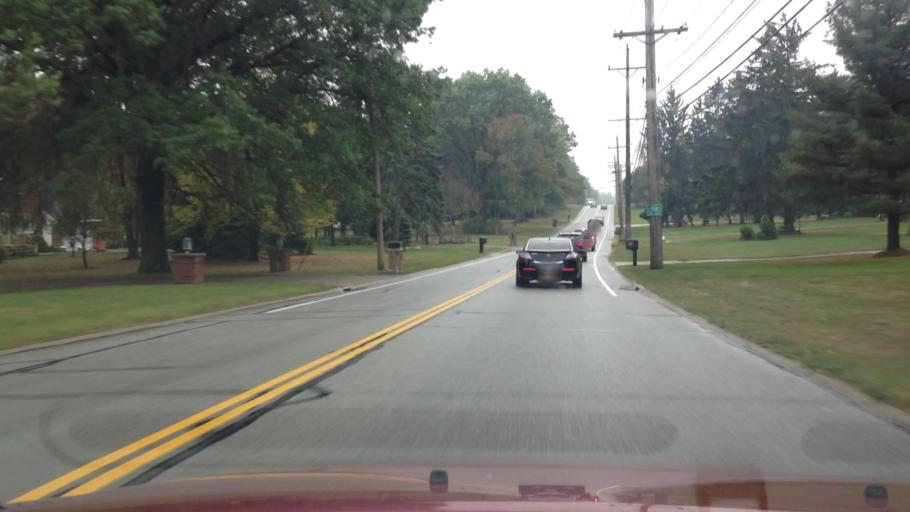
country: US
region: Ohio
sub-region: Cuyahoga County
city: Mayfield Heights
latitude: 41.5001
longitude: -81.4630
